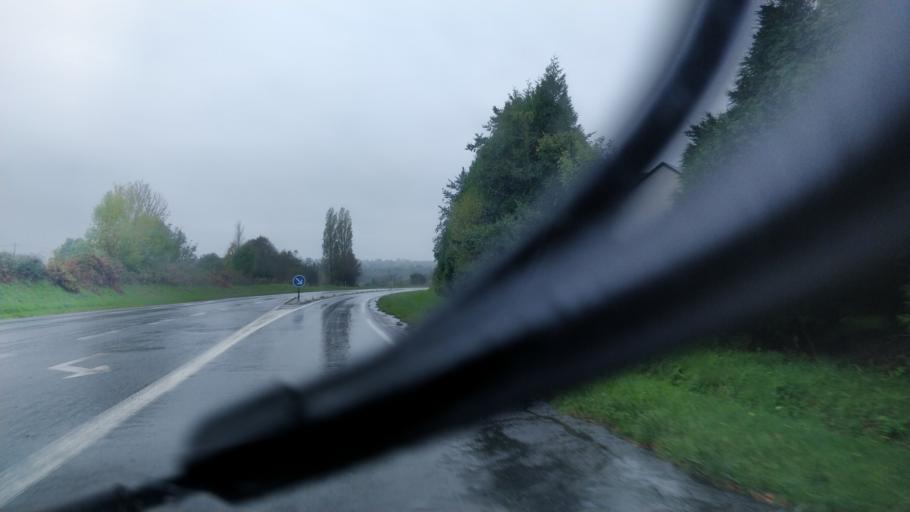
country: FR
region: Lower Normandy
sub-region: Departement de la Manche
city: Saint-Planchers
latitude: 48.8615
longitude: -1.5386
